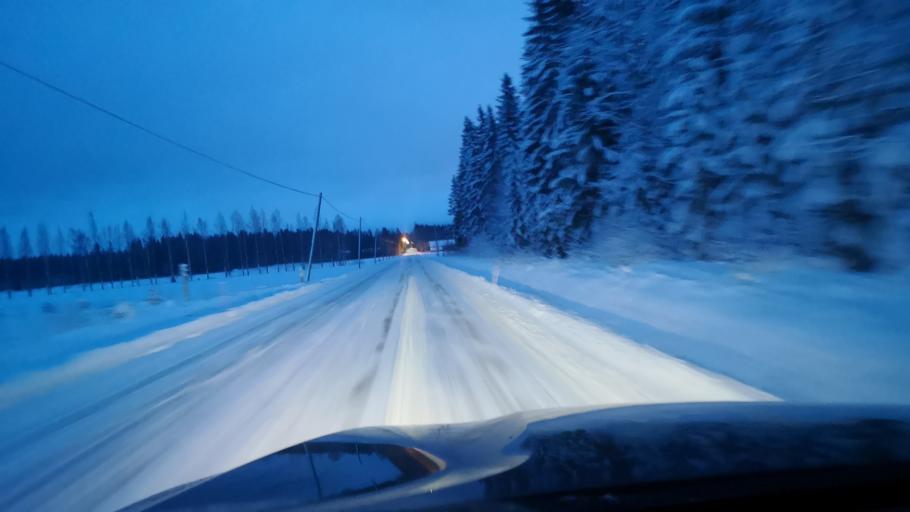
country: FI
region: Varsinais-Suomi
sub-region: Loimaa
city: Loimaa
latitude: 60.8781
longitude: 23.0895
